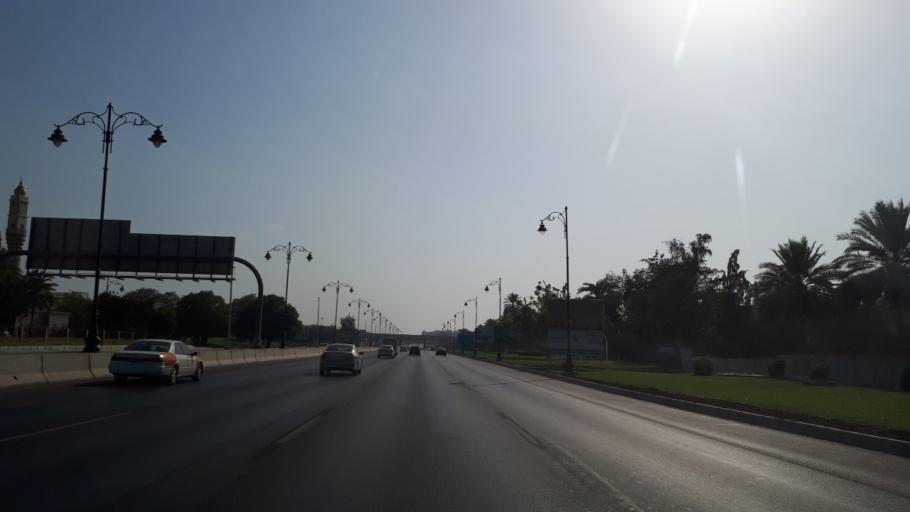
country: OM
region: Muhafazat Masqat
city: Bawshar
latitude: 23.6143
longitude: 58.4777
